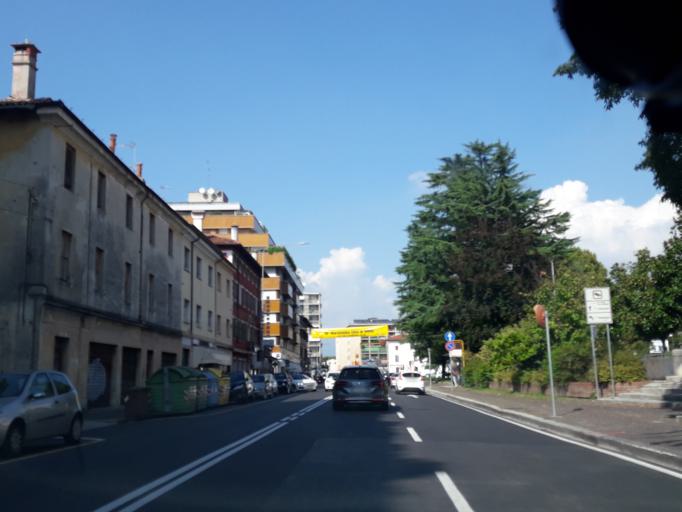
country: IT
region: Friuli Venezia Giulia
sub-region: Provincia di Udine
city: Udine
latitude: 46.0763
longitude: 13.2347
